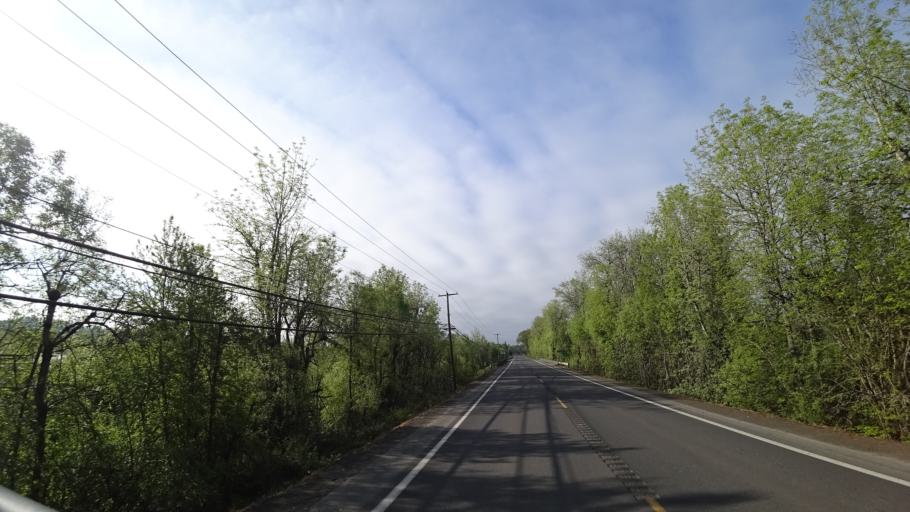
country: US
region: Oregon
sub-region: Washington County
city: Hillsboro
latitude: 45.5061
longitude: -122.9910
